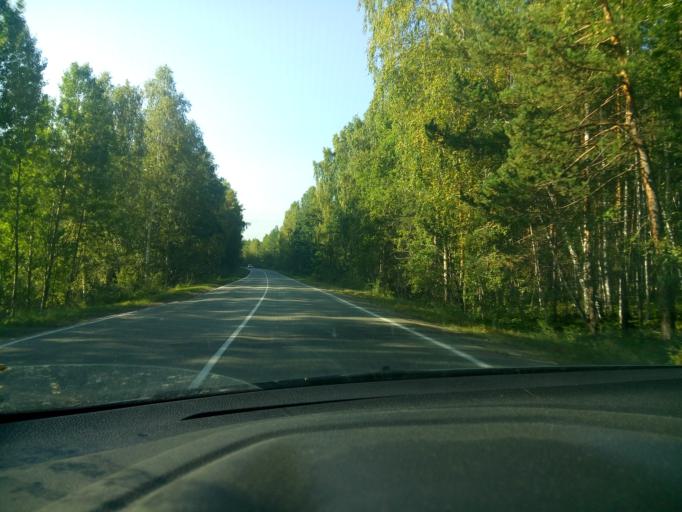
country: RU
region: Chelyabinsk
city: Ozersk
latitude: 55.8380
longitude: 60.6495
